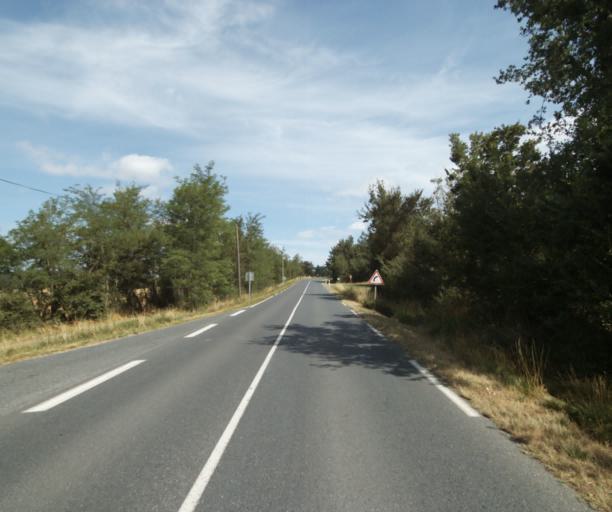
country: FR
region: Midi-Pyrenees
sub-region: Departement du Tarn
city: Dourgne
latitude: 43.4770
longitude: 2.1091
